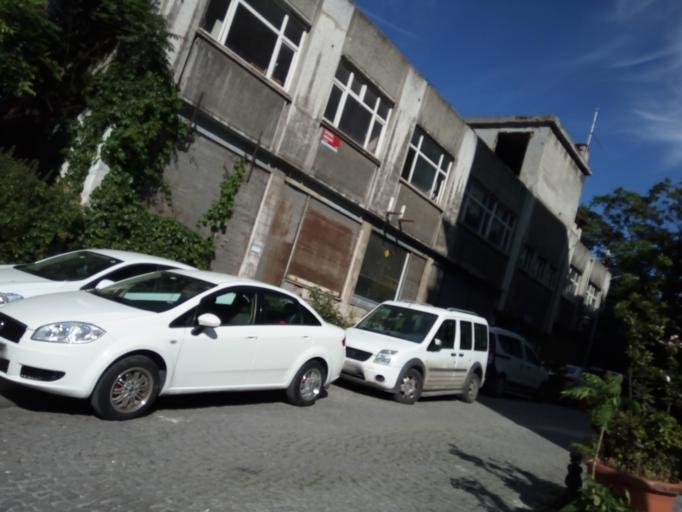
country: TR
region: Istanbul
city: Eminoenue
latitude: 41.0103
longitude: 28.9771
